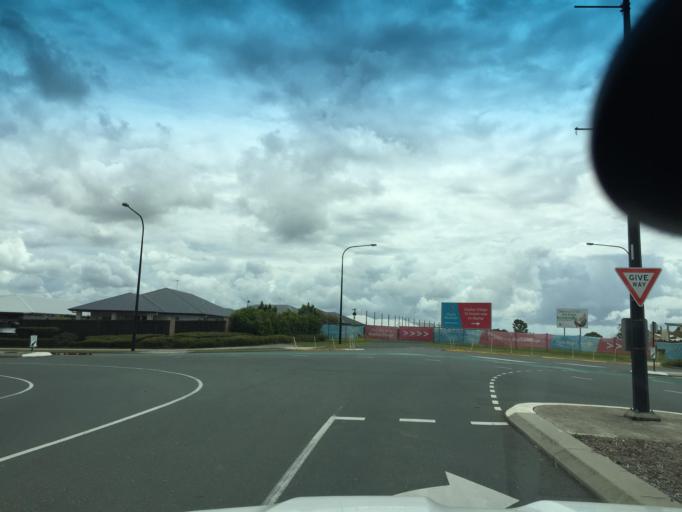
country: AU
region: Queensland
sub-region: Moreton Bay
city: Morayfield
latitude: -27.1215
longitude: 152.9961
